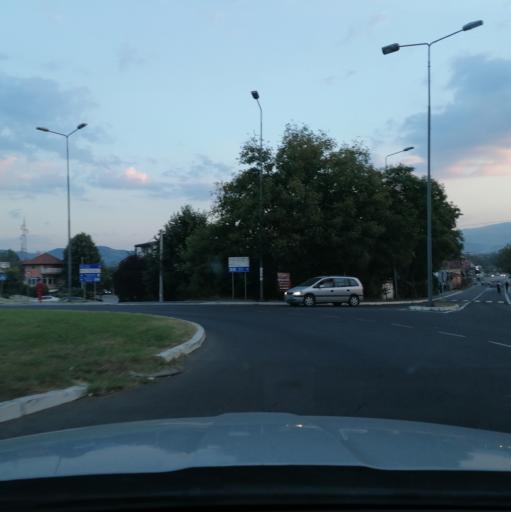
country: RS
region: Central Serbia
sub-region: Raski Okrug
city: Kraljevo
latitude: 43.7127
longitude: 20.6942
